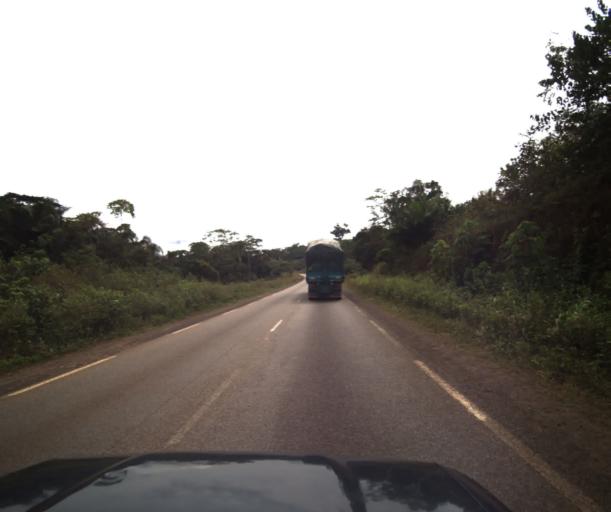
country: CM
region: Littoral
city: Edea
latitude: 3.8171
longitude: 10.3698
